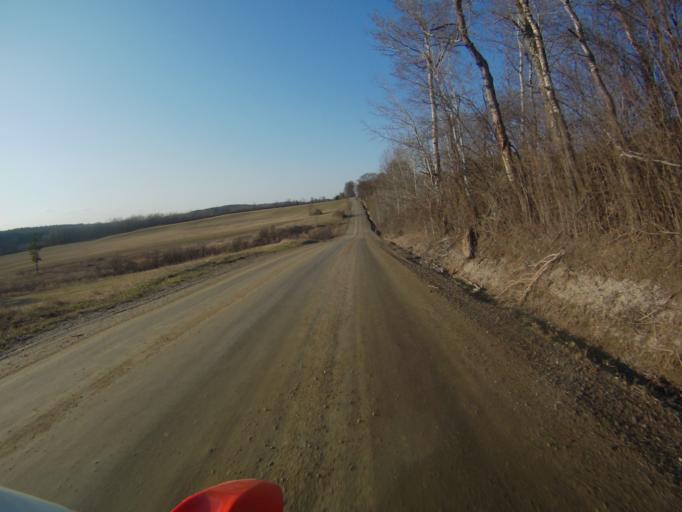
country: US
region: Vermont
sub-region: Addison County
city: Bristol
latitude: 44.1014
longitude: -73.0880
